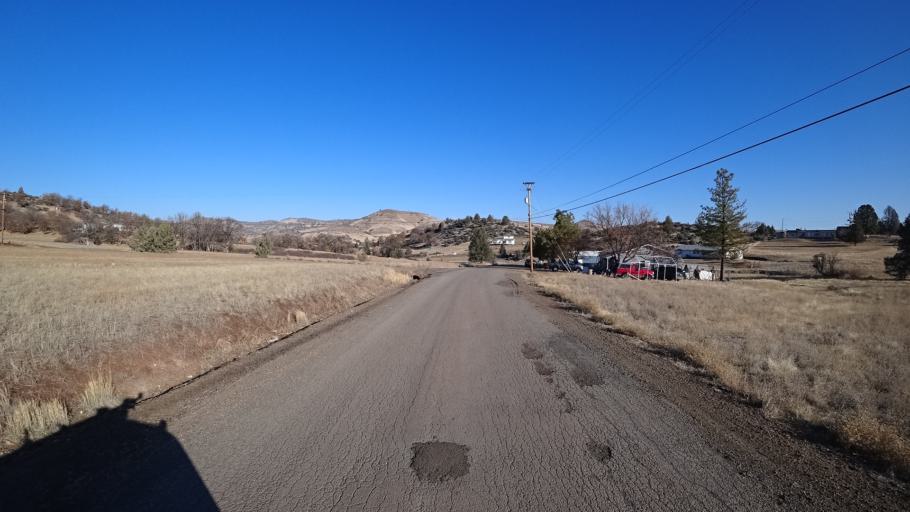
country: US
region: California
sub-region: Siskiyou County
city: Montague
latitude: 41.8895
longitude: -122.4915
